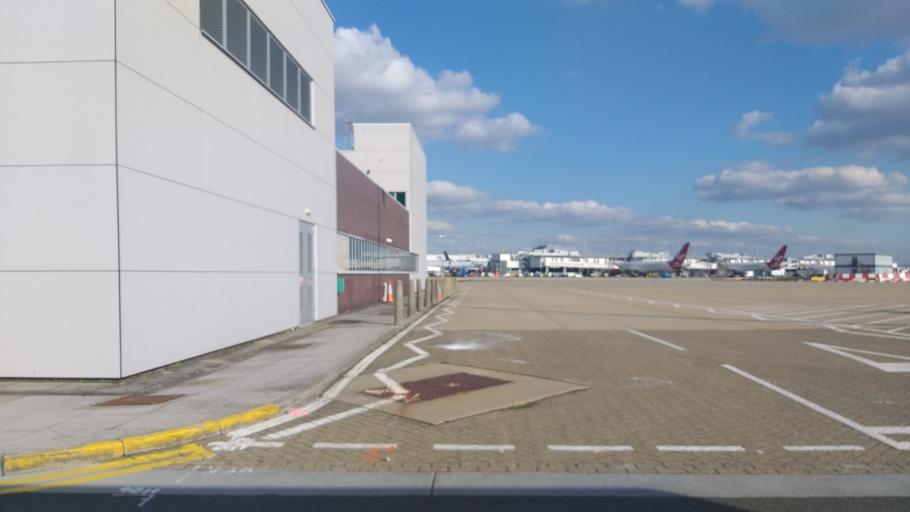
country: GB
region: England
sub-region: Greater London
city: West Drayton
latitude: 51.4708
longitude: -0.4707
